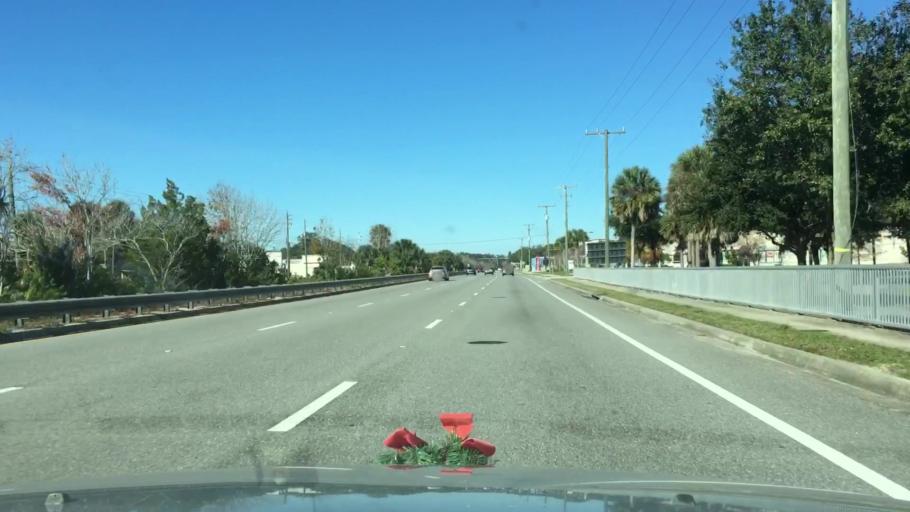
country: US
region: Florida
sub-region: Volusia County
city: South Daytona
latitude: 29.1511
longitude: -81.0176
